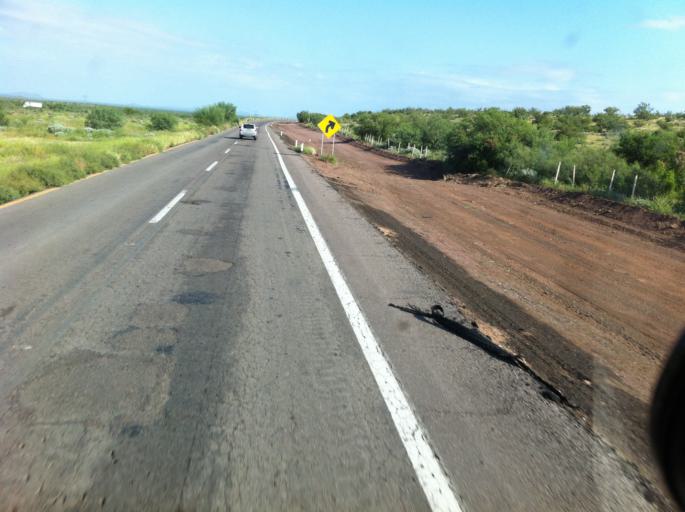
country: MX
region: Sonora
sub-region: Hermosillo
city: Miguel Aleman (La Doce)
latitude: 28.5009
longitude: -111.0444
